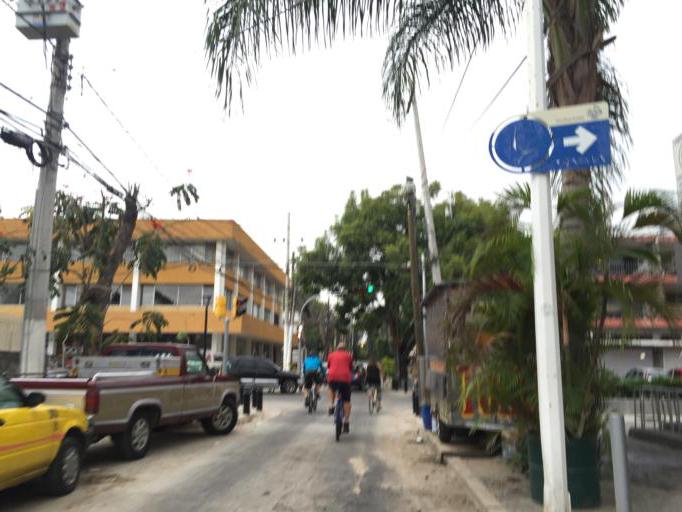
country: MX
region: Jalisco
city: Guadalajara
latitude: 20.6735
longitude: -103.3706
